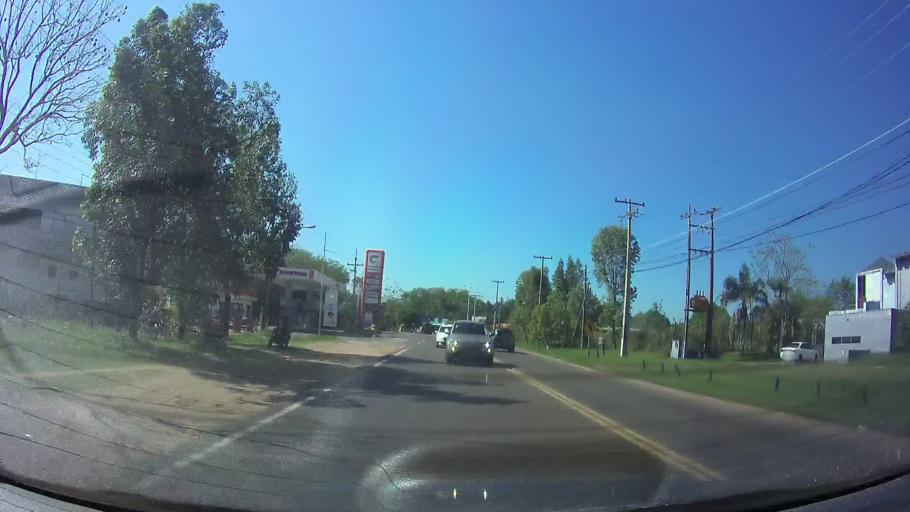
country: PY
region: Cordillera
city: San Bernardino
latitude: -25.3376
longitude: -57.2729
